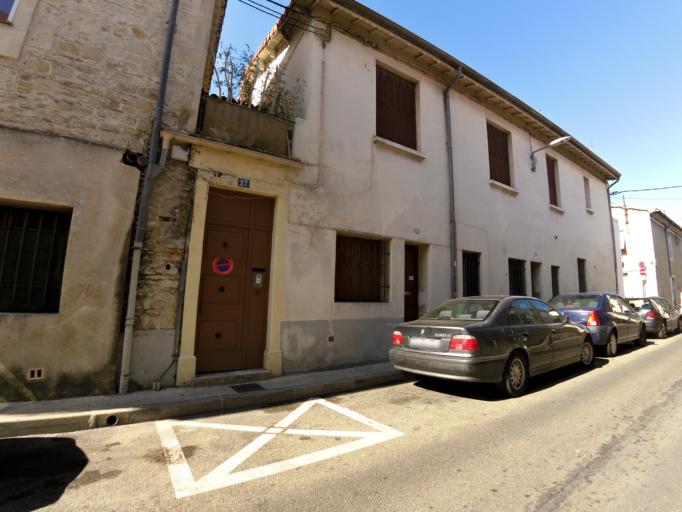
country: FR
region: Languedoc-Roussillon
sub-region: Departement du Gard
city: Nimes
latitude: 43.8302
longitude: 4.3549
